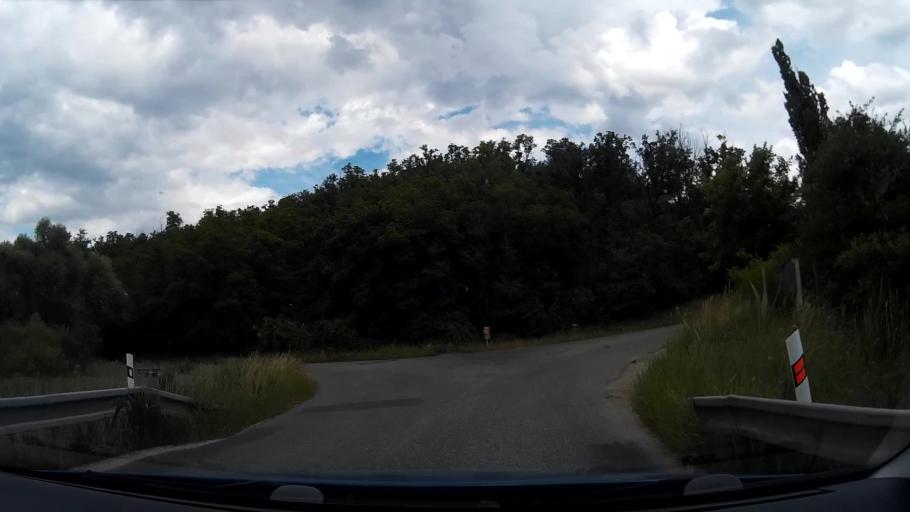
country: CZ
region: South Moravian
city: Ostopovice
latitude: 49.1453
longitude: 16.5311
